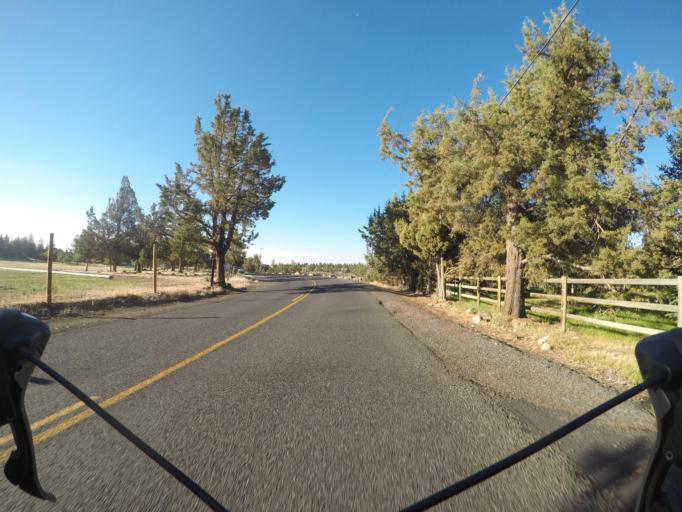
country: US
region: Oregon
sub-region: Deschutes County
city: Redmond
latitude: 44.2685
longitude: -121.2509
